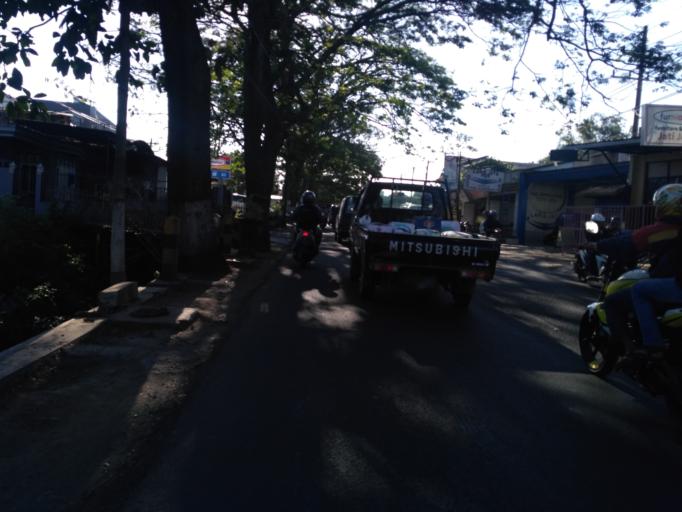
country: ID
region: East Java
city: Batu
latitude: -7.8942
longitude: 112.5517
